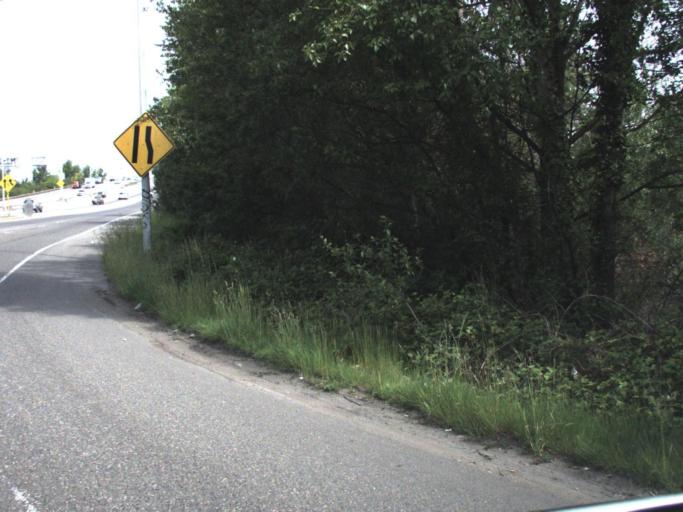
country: US
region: Washington
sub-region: Pierce County
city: Fife
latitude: 47.2420
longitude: -122.3570
